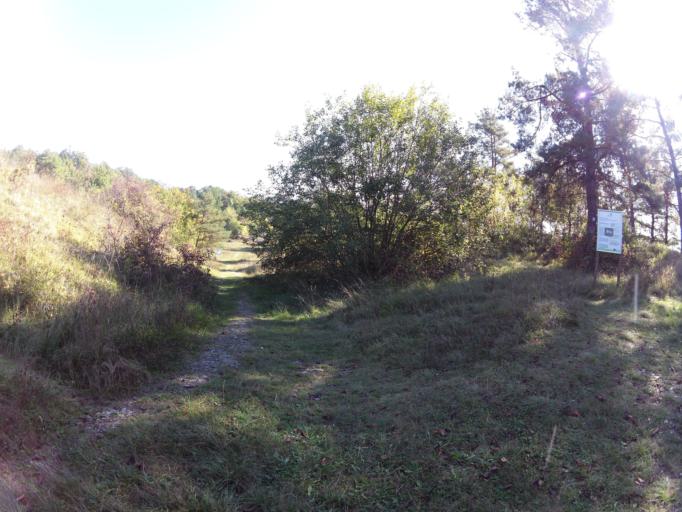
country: DE
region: Bavaria
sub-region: Regierungsbezirk Unterfranken
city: Sommerhausen
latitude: 49.6818
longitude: 10.0391
